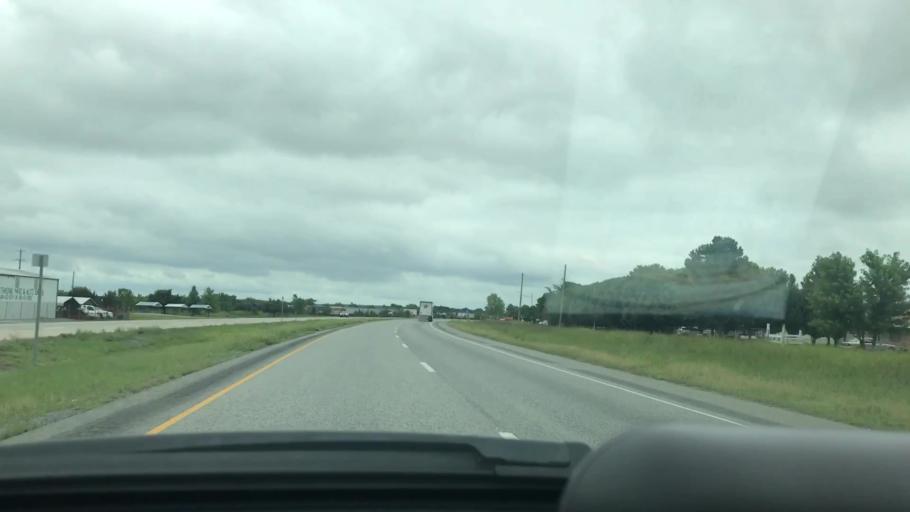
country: US
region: Oklahoma
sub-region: Pittsburg County
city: McAlester
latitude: 34.7331
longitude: -95.8996
